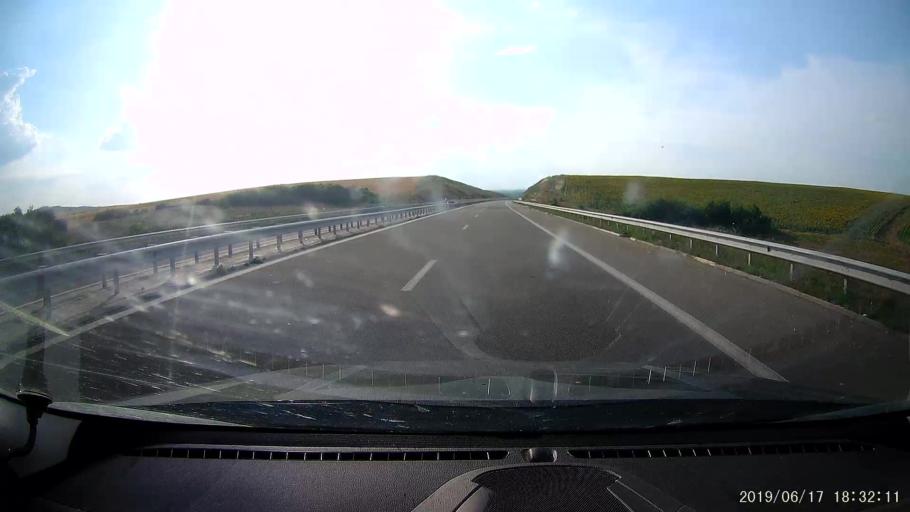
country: BG
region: Khaskovo
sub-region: Obshtina Dimitrovgrad
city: Dimitrovgrad
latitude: 42.0560
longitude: 25.4850
